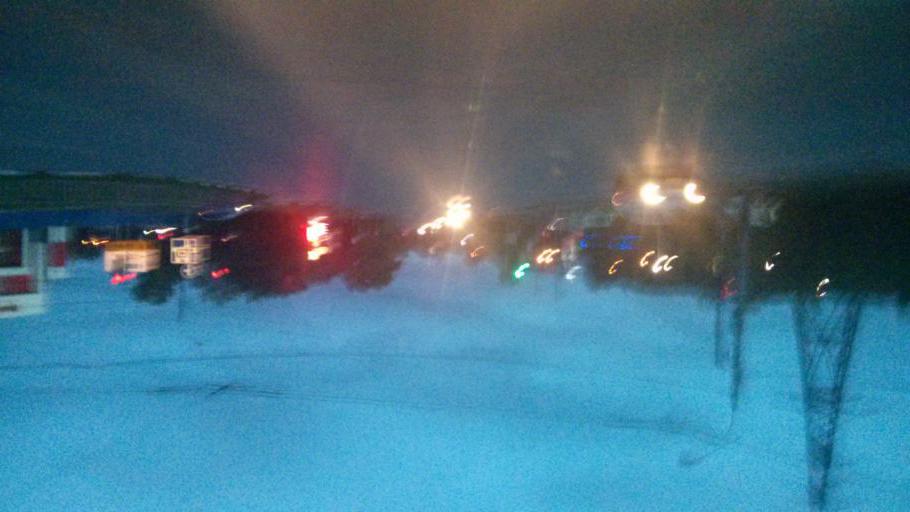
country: RU
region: Nizjnij Novgorod
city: Nizhniy Novgorod
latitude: 56.2297
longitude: 43.9447
